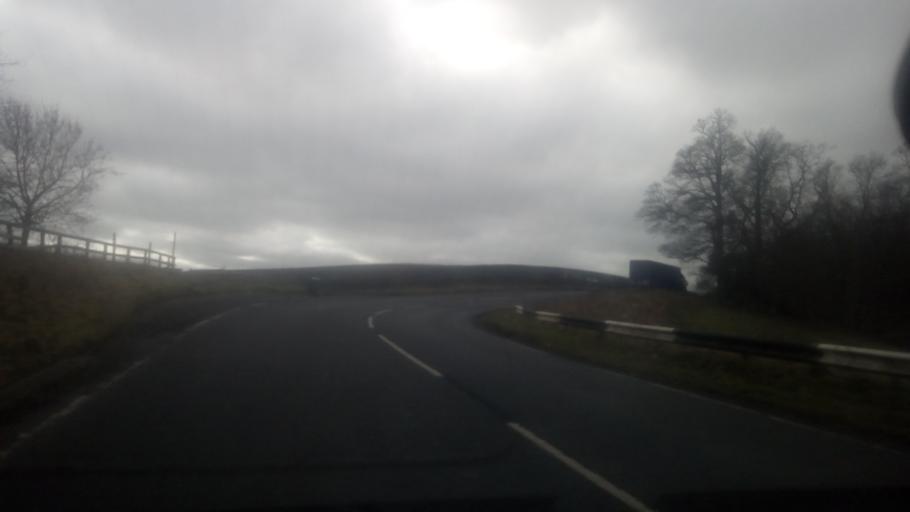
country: GB
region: Scotland
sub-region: The Scottish Borders
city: Kelso
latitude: 55.5954
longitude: -2.4595
